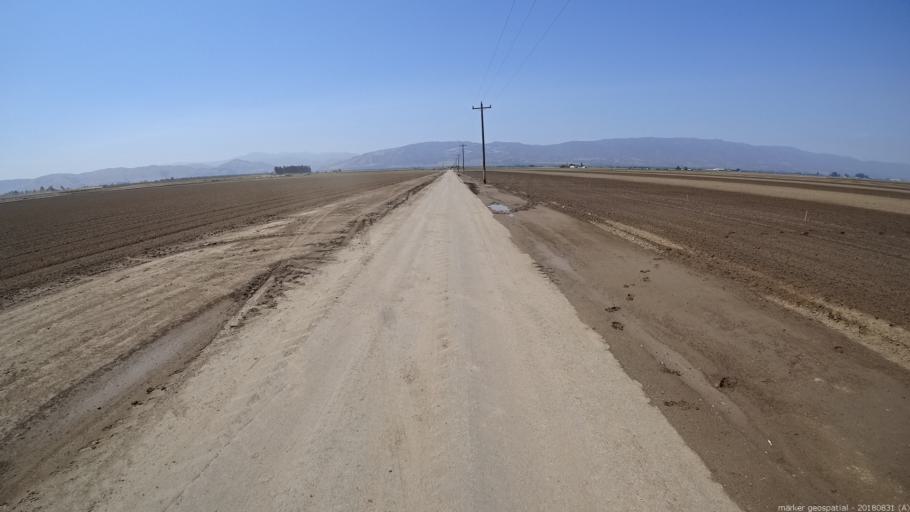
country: US
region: California
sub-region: Monterey County
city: Greenfield
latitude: 36.3579
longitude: -121.2566
